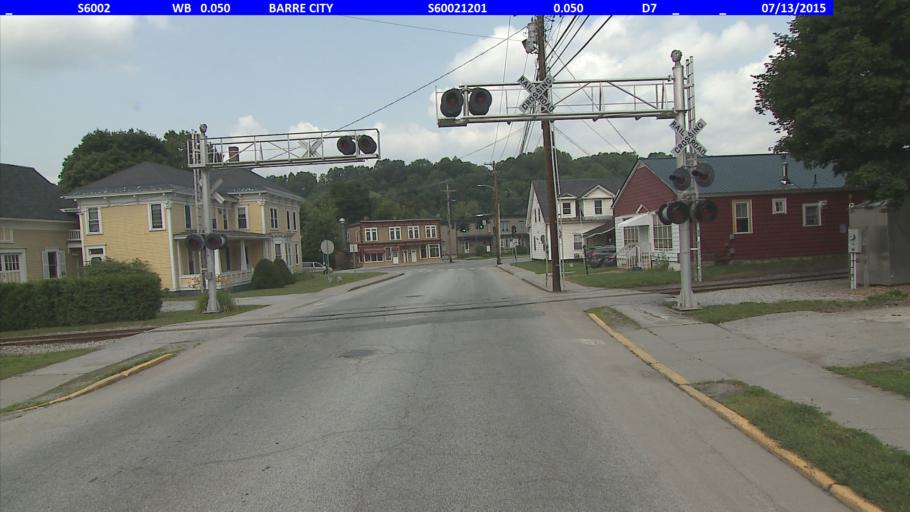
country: US
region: Vermont
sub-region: Washington County
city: Barre
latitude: 44.1908
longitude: -72.4977
